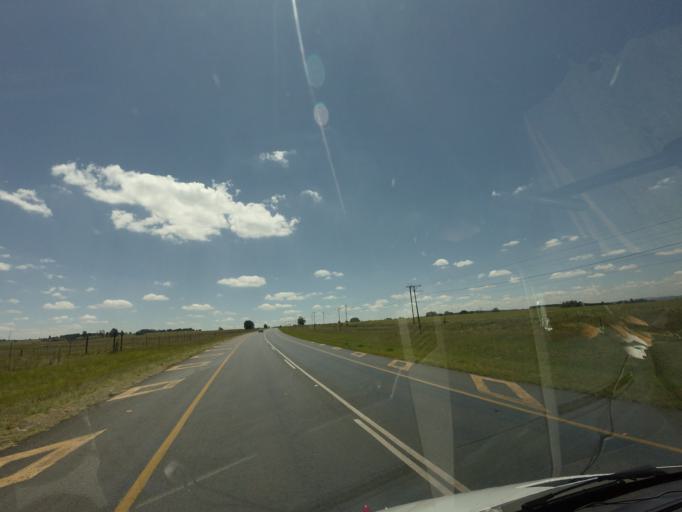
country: ZA
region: Mpumalanga
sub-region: Nkangala District Municipality
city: Belfast
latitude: -25.7220
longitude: 30.0817
